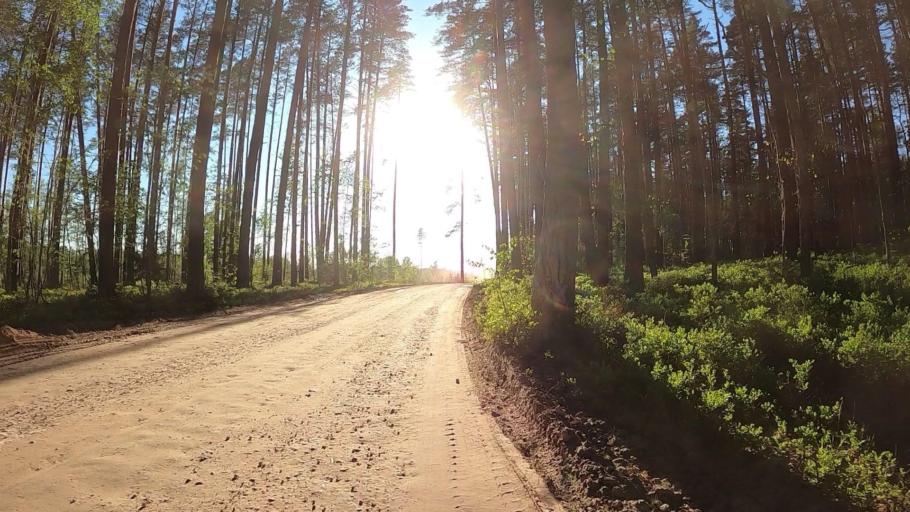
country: LV
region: Kekava
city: Kekava
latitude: 56.7821
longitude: 24.3057
